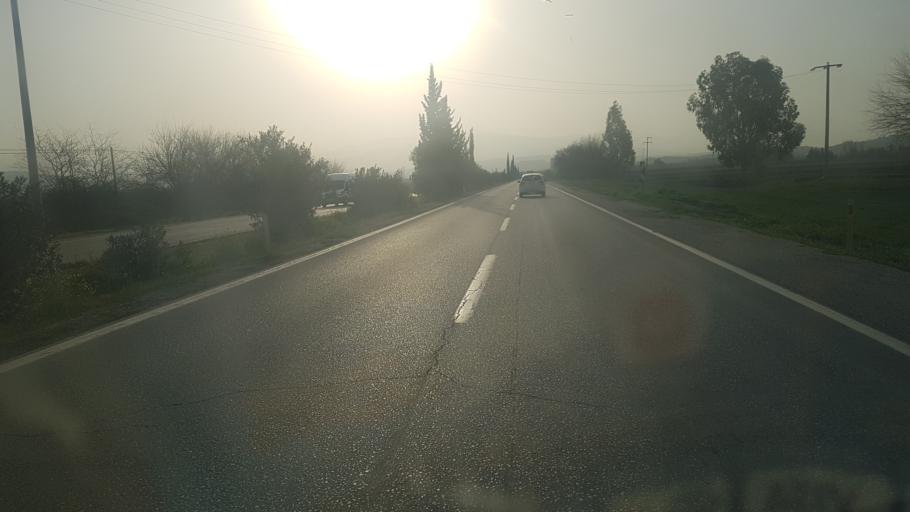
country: TR
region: Osmaniye
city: Toprakkale
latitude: 37.0687
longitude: 36.0963
